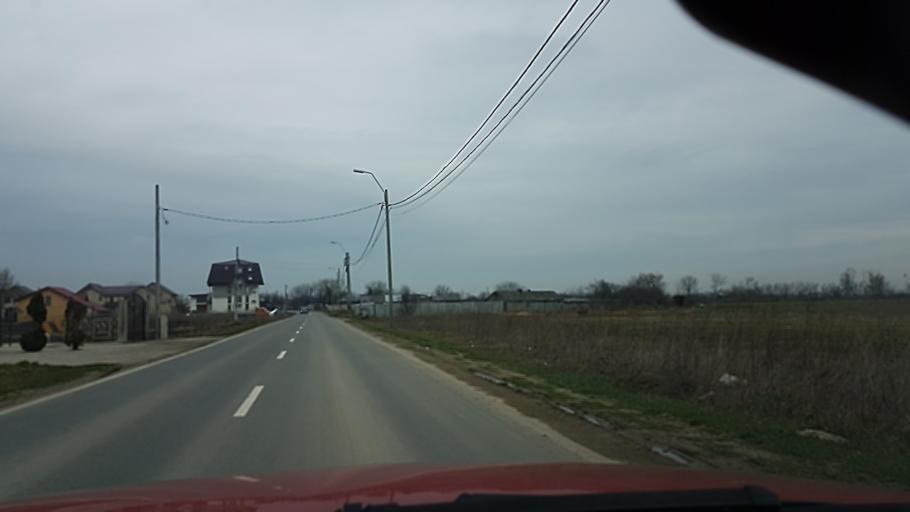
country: RO
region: Ilfov
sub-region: Comuna Balotesti
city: Balotesti
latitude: 44.5966
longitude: 26.1339
